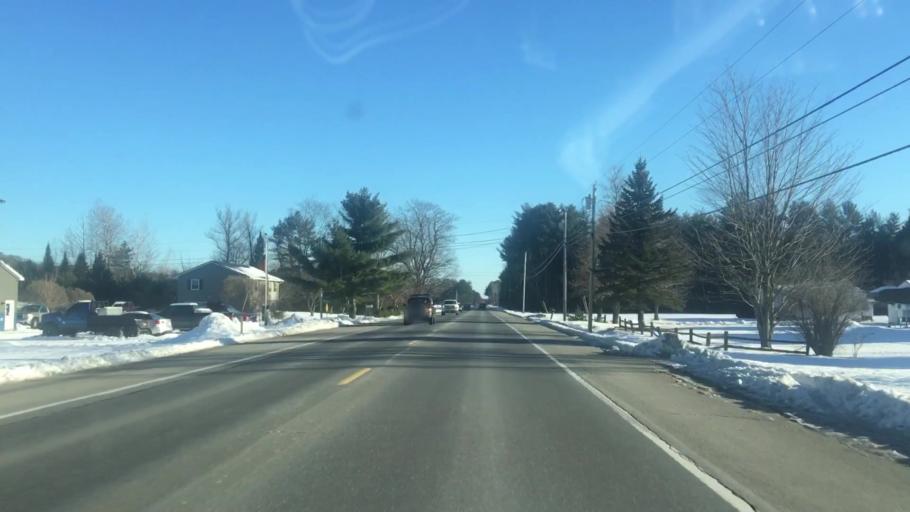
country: US
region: Maine
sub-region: Somerset County
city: Norridgewock
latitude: 44.7048
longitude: -69.7694
